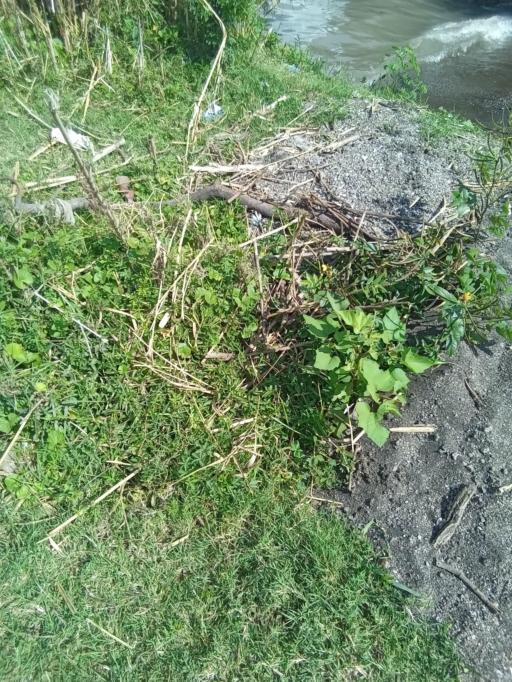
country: KE
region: Homa Bay
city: Homa Bay
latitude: -0.4574
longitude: 34.1924
